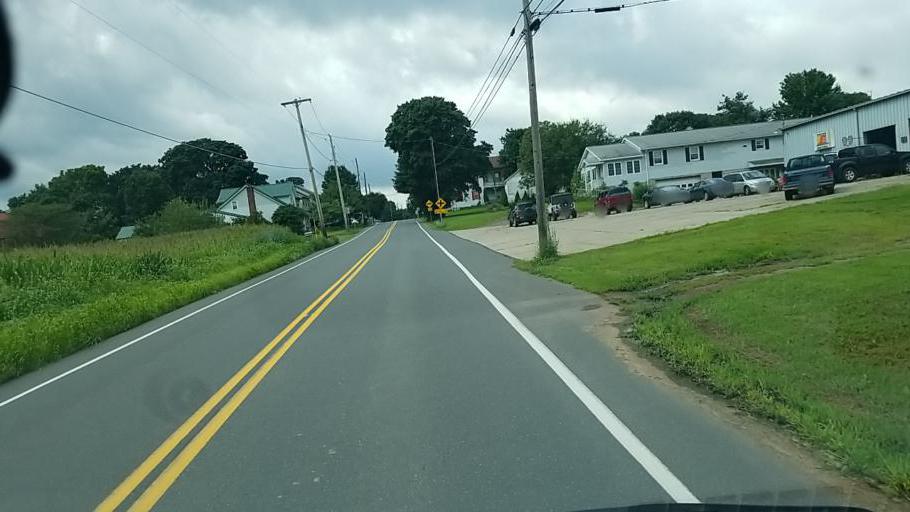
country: US
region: Pennsylvania
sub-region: Dauphin County
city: Matamoras
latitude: 40.5020
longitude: -76.8837
